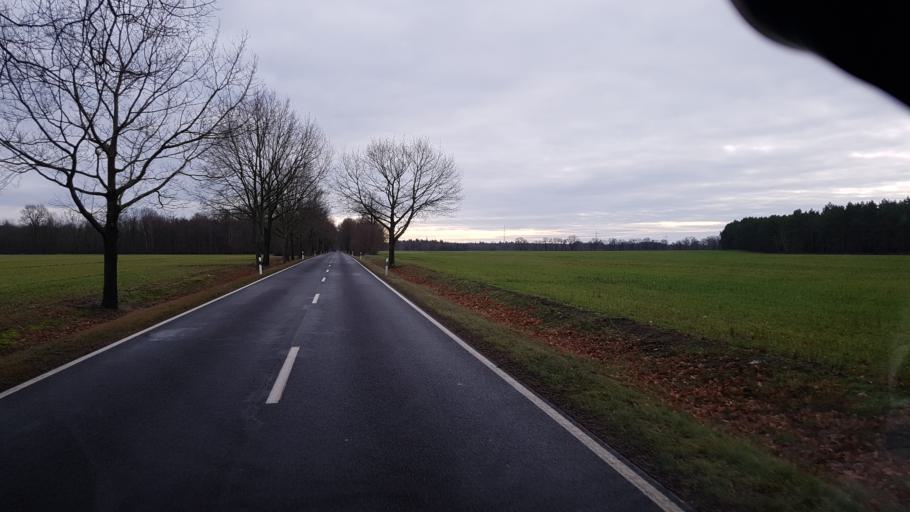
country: DE
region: Brandenburg
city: Altdobern
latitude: 51.6807
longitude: 14.0273
